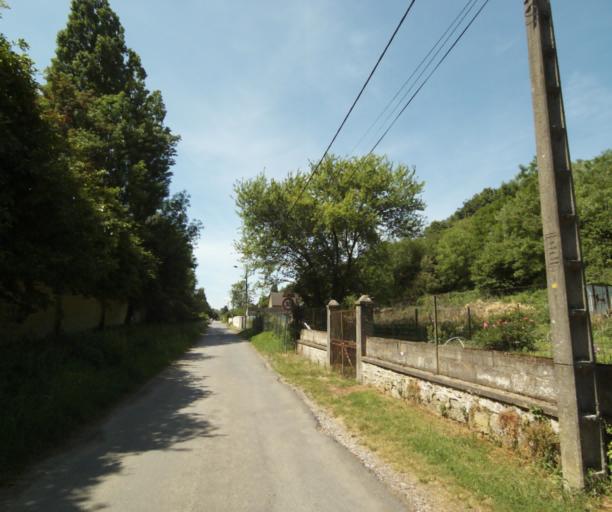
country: FR
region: Champagne-Ardenne
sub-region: Departement des Ardennes
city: Charleville-Mezieres
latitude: 49.7721
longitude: 4.7032
